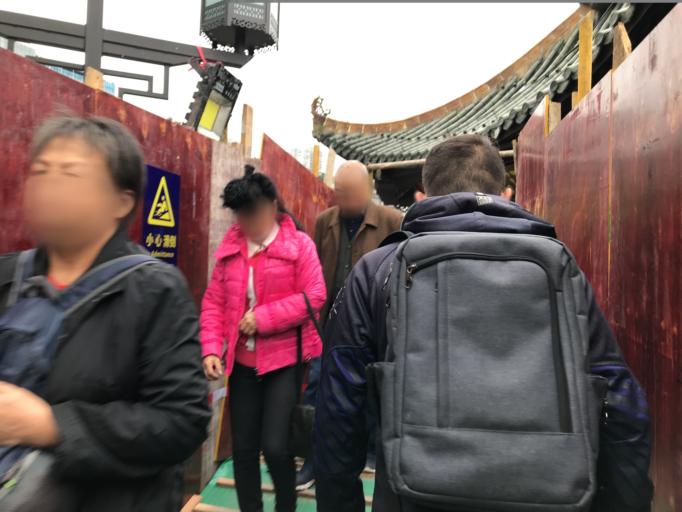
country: CN
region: Guizhou Sheng
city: Guiyang
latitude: 26.5753
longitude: 106.7156
